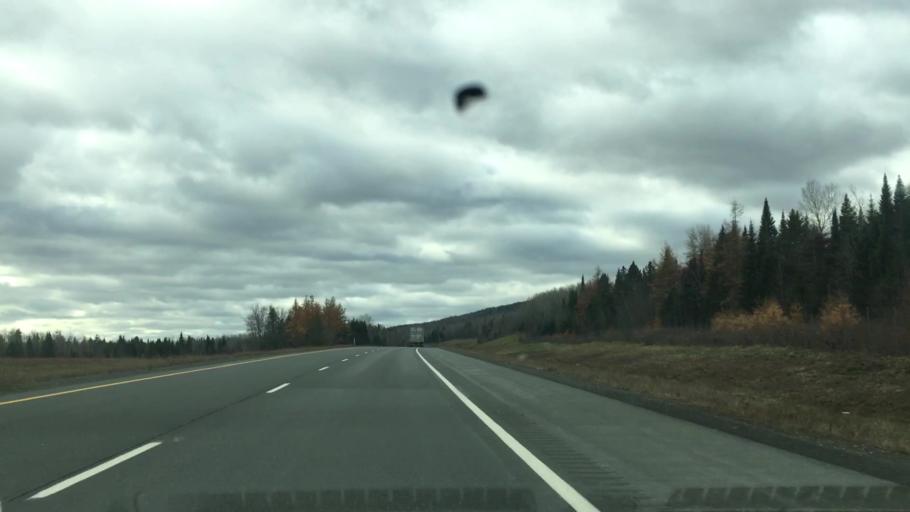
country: US
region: Maine
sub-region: Aroostook County
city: Fort Fairfield
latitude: 46.6579
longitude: -67.7351
